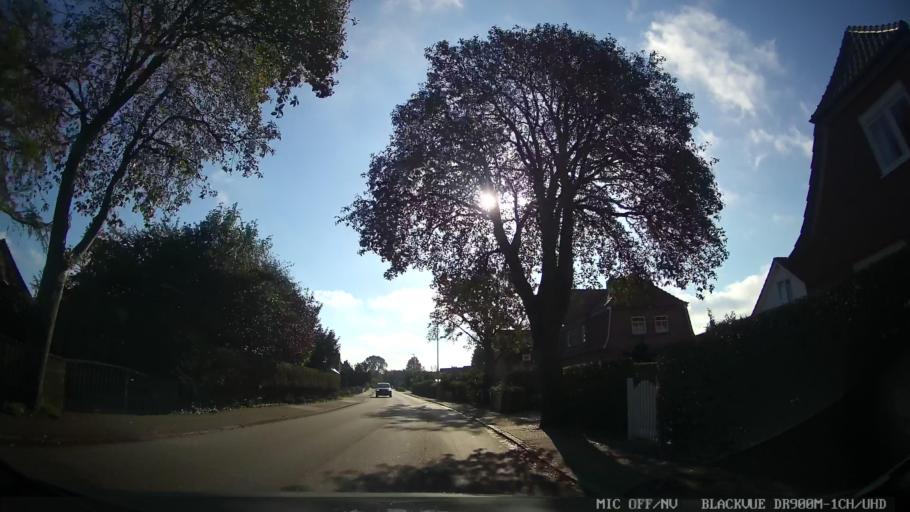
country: DE
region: Schleswig-Holstein
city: Heiligenhafen
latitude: 54.3699
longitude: 10.9888
